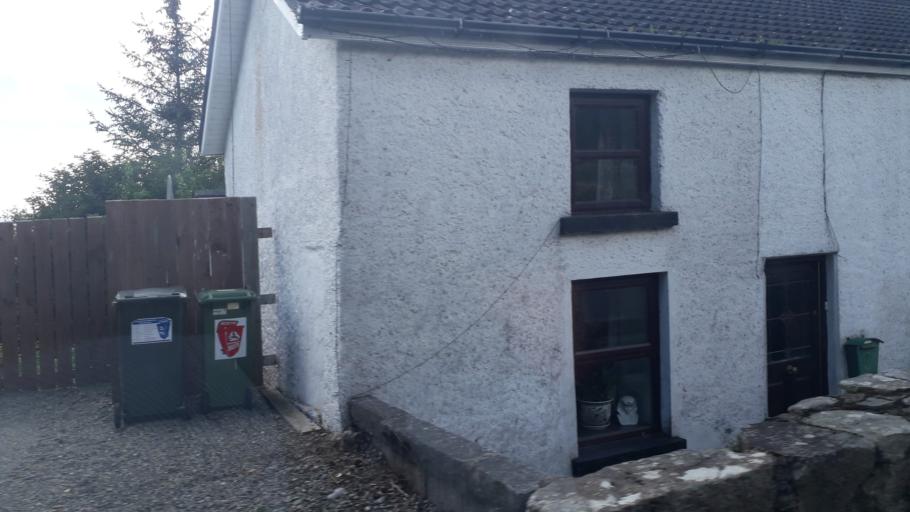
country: IE
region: Leinster
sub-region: Lu
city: Blackrock
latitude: 54.0420
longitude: -6.3308
